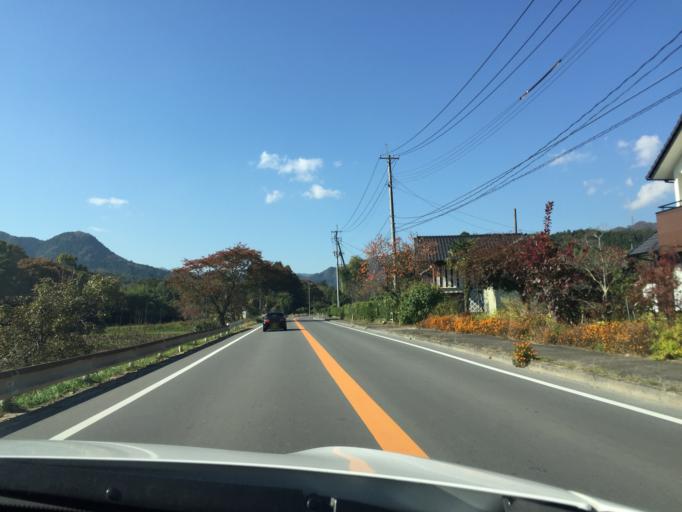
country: JP
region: Miyagi
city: Marumori
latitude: 37.7768
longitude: 140.8926
